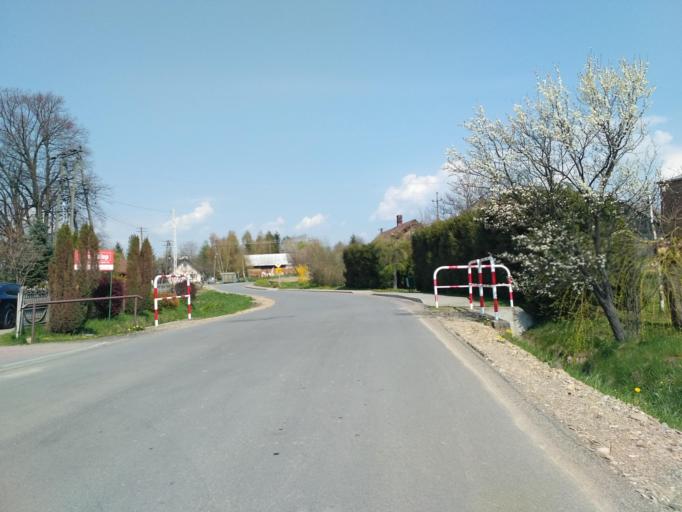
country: PL
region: Subcarpathian Voivodeship
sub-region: Powiat krosnienski
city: Chorkowka
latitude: 49.6318
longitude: 21.6997
